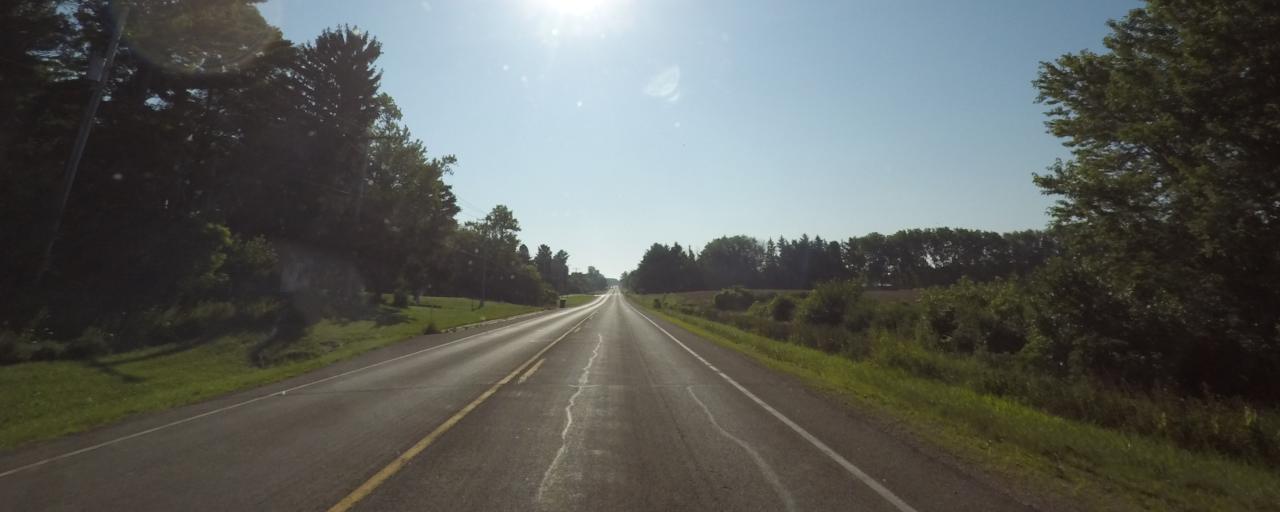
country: US
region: Wisconsin
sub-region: Jefferson County
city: Fort Atkinson
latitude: 42.9390
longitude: -88.7668
